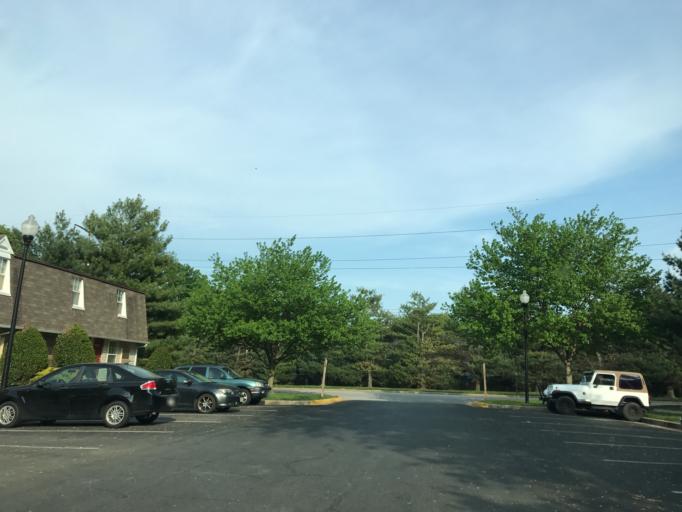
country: US
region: Maryland
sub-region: Baltimore County
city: Middle River
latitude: 39.3376
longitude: -76.4392
